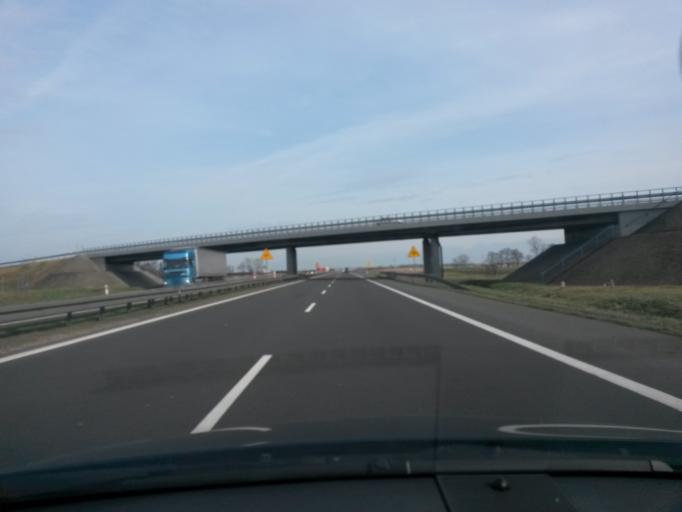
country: PL
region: Greater Poland Voivodeship
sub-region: Powiat poznanski
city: Swarzedz
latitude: 52.3353
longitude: 17.0615
